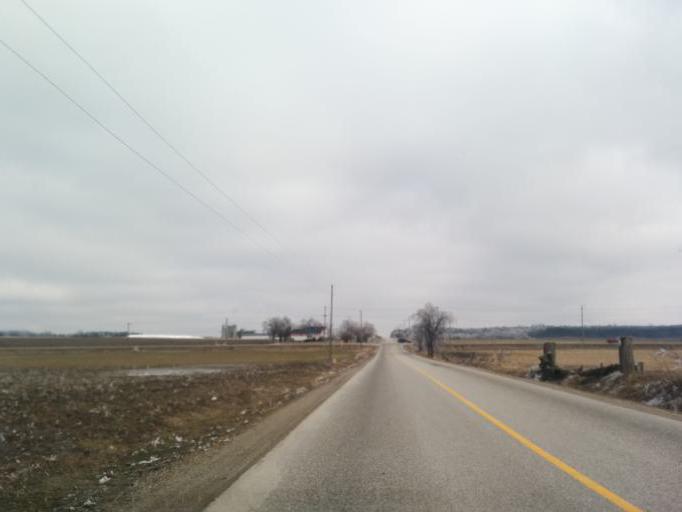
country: CA
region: Ontario
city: Waterloo
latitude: 43.6489
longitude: -80.5494
